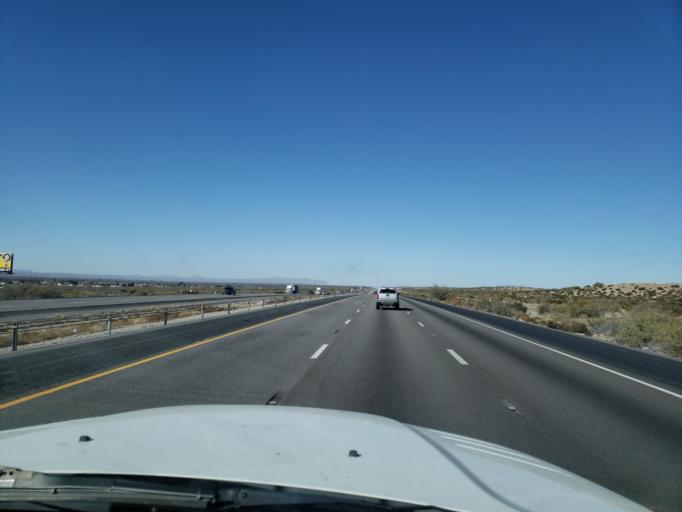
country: US
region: New Mexico
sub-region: Dona Ana County
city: Mesquite
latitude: 32.2006
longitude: -106.6889
